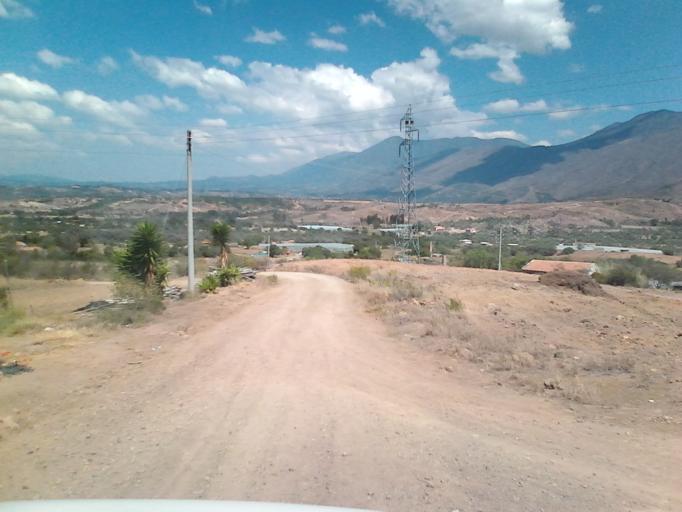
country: CO
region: Boyaca
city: Sachica
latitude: 5.6031
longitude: -73.5669
